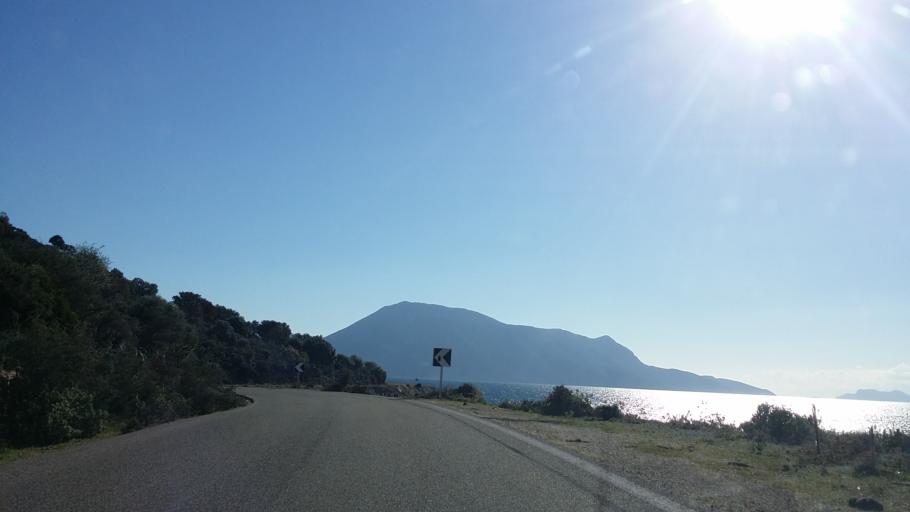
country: GR
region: West Greece
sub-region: Nomos Aitolias kai Akarnanias
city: Kandila
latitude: 38.7095
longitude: 20.8940
